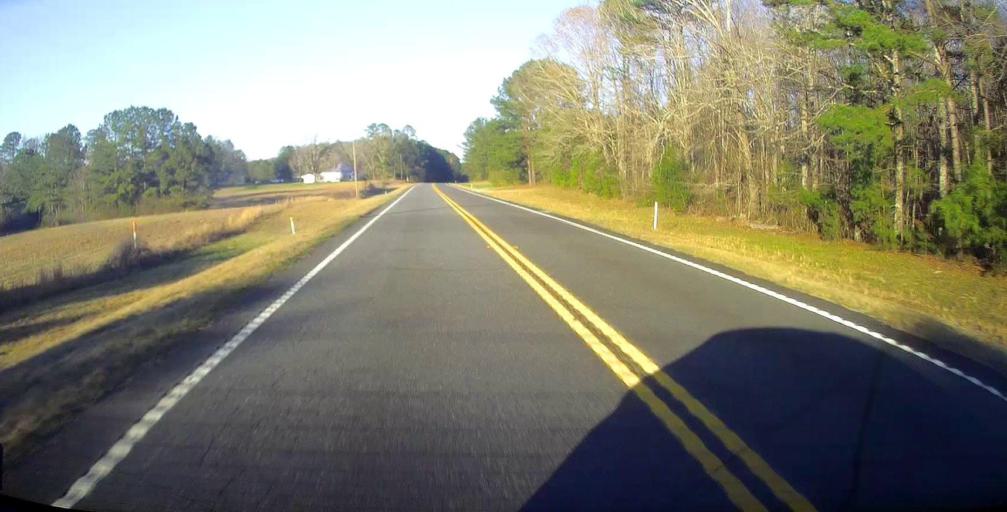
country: US
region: Georgia
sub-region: Talbot County
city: Talbotton
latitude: 32.6698
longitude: -84.6142
